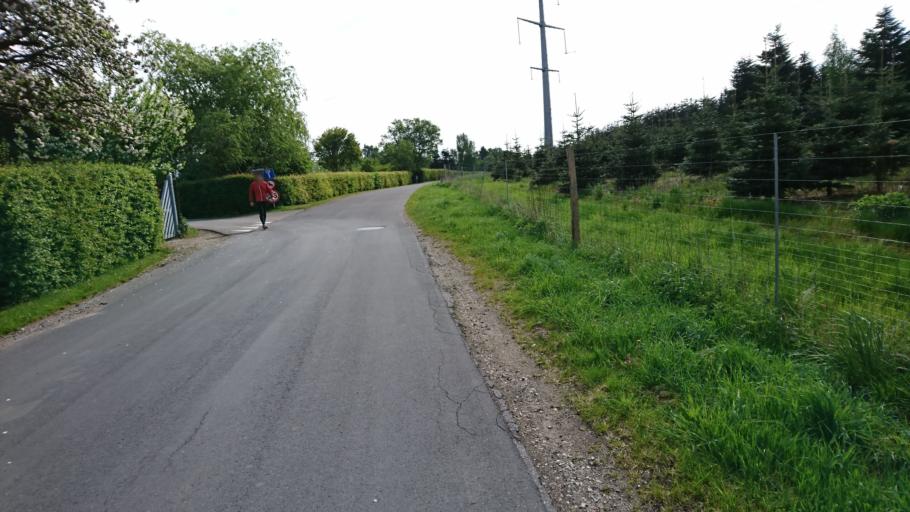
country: DK
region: Capital Region
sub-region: Egedal Kommune
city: Smorumnedre
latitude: 55.7309
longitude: 12.3164
